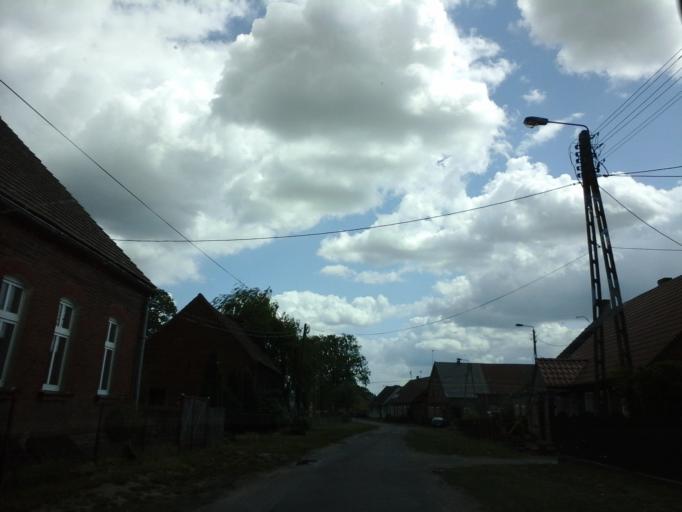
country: PL
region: West Pomeranian Voivodeship
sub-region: Powiat choszczenski
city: Choszczno
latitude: 53.1301
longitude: 15.3776
